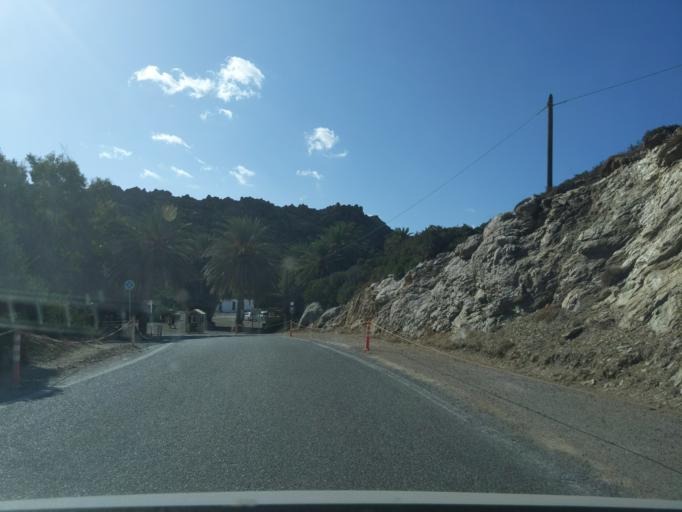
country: GR
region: Crete
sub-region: Nomos Lasithiou
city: Palekastro
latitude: 35.2538
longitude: 26.2643
